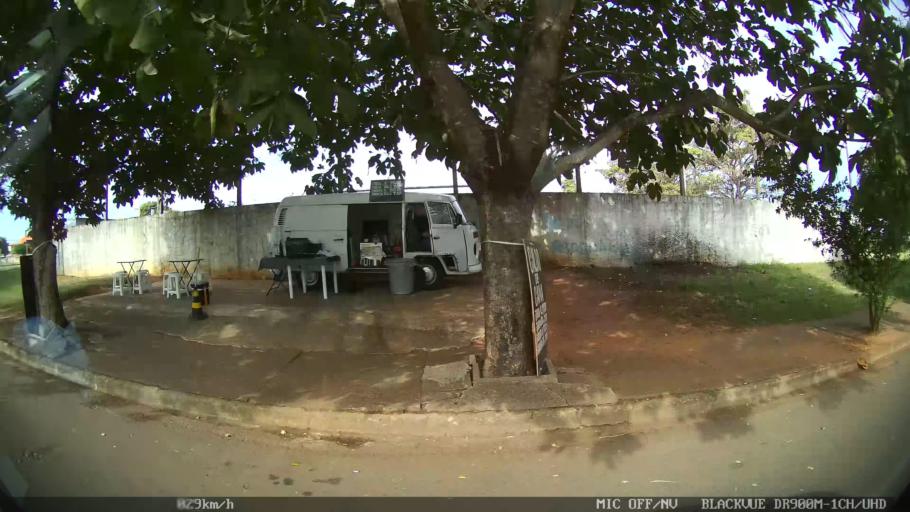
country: BR
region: Sao Paulo
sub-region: Santa Barbara D'Oeste
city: Santa Barbara d'Oeste
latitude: -22.7713
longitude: -47.3893
